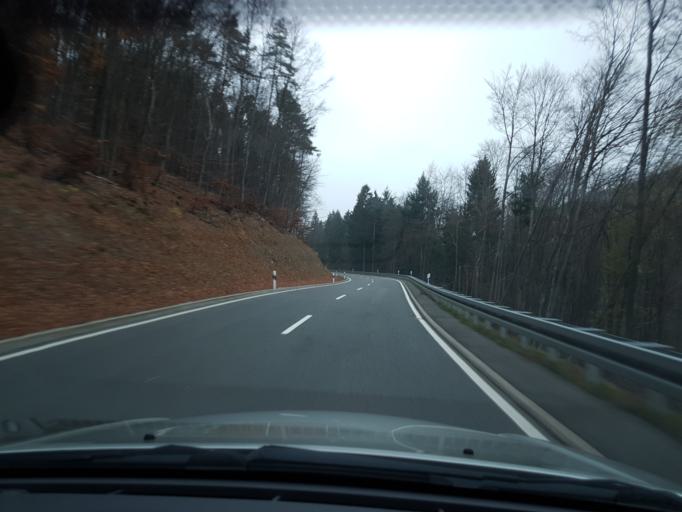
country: DE
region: Hesse
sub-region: Regierungsbezirk Darmstadt
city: Kiedrich
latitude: 50.0681
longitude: 8.0595
